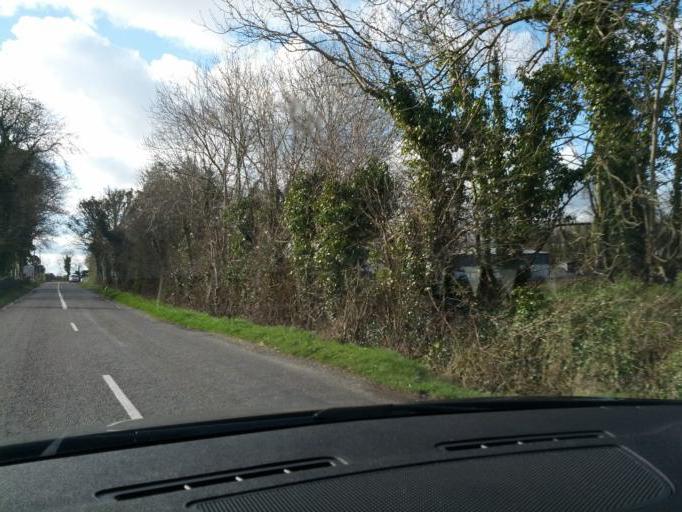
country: IE
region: Connaught
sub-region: Roscommon
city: Castlerea
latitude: 53.5145
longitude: -8.5768
